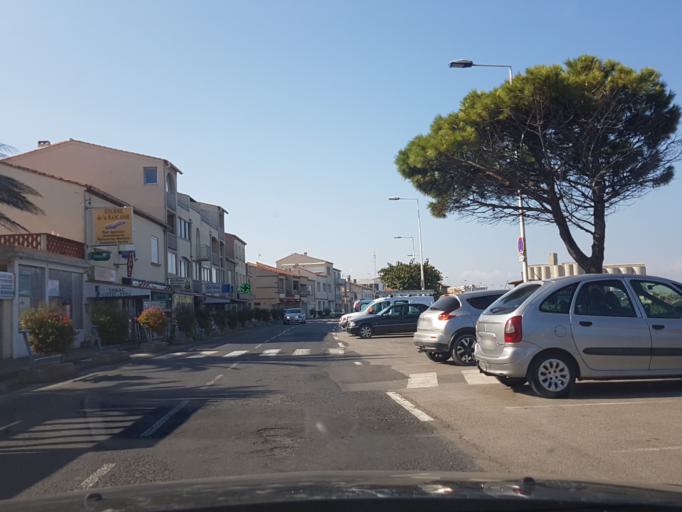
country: FR
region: Languedoc-Roussillon
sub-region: Departement de l'Aude
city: Port-la-Nouvelle
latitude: 43.0150
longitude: 3.0620
